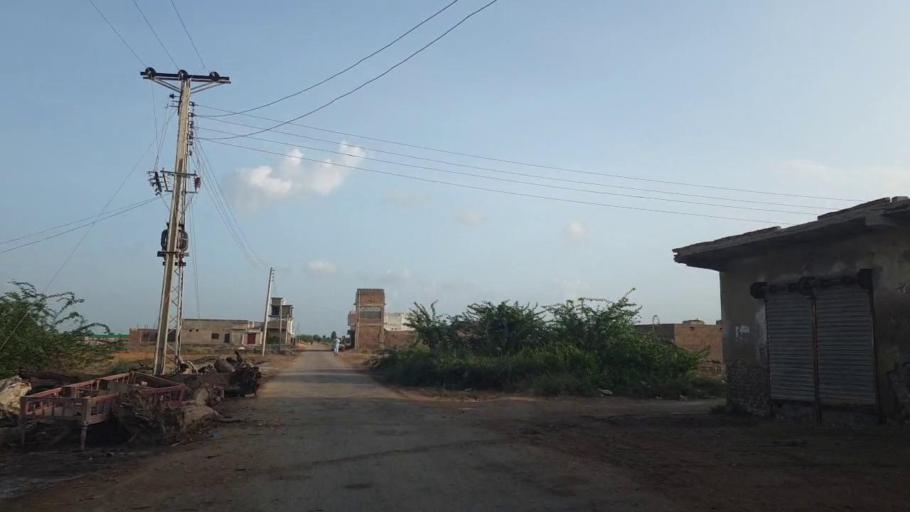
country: PK
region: Sindh
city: Kadhan
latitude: 24.6394
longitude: 69.1228
